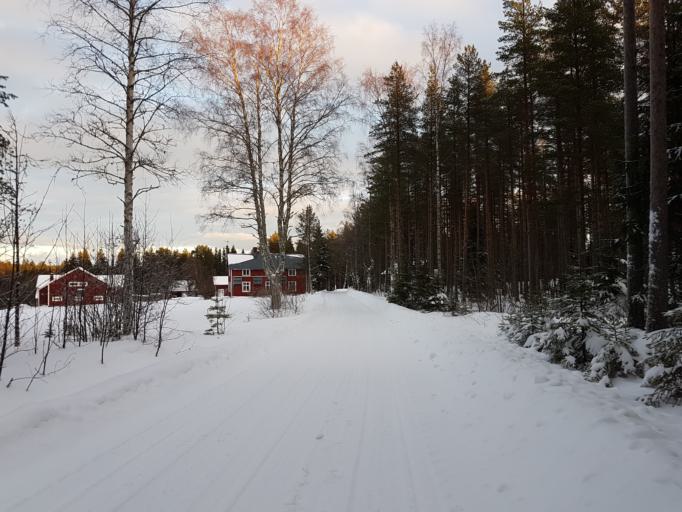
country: SE
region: Vaesterbotten
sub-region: Robertsfors Kommun
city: Robertsfors
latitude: 64.0467
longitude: 20.8701
